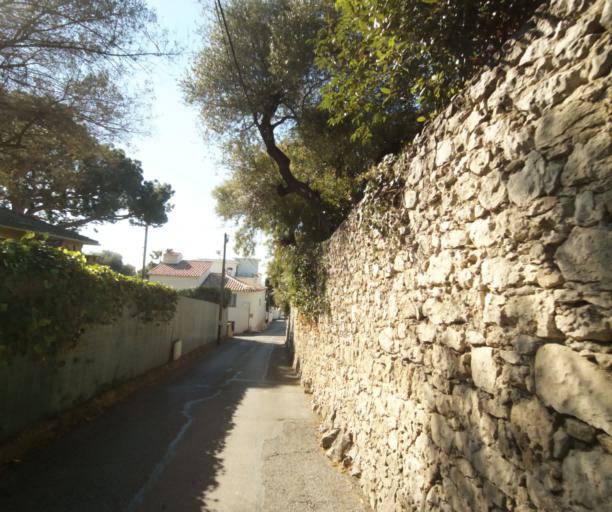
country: FR
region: Provence-Alpes-Cote d'Azur
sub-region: Departement des Alpes-Maritimes
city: Antibes
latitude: 43.5625
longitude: 7.1191
